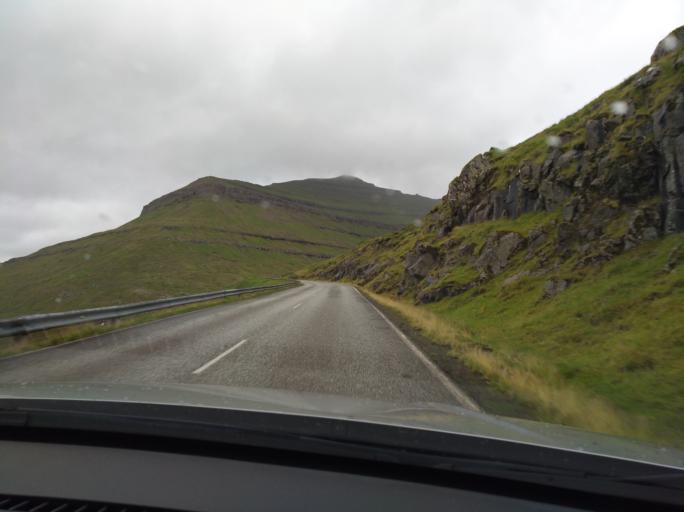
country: FO
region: Eysturoy
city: Fuglafjordur
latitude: 62.2207
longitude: -6.8715
